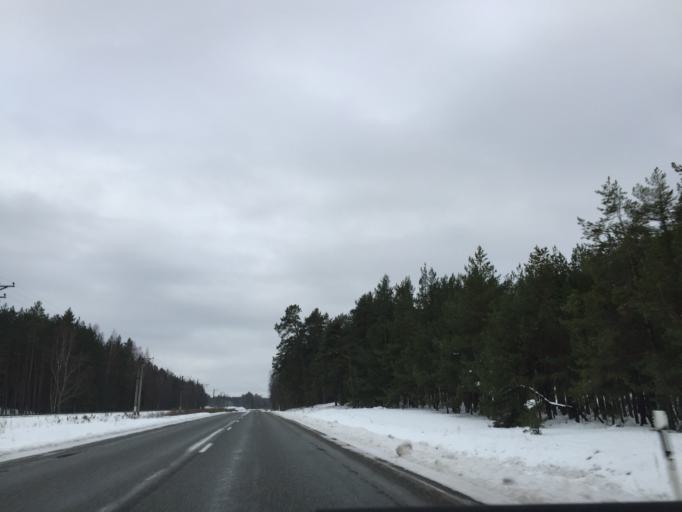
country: LV
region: Saulkrastu
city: Saulkrasti
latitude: 57.2031
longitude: 24.3730
